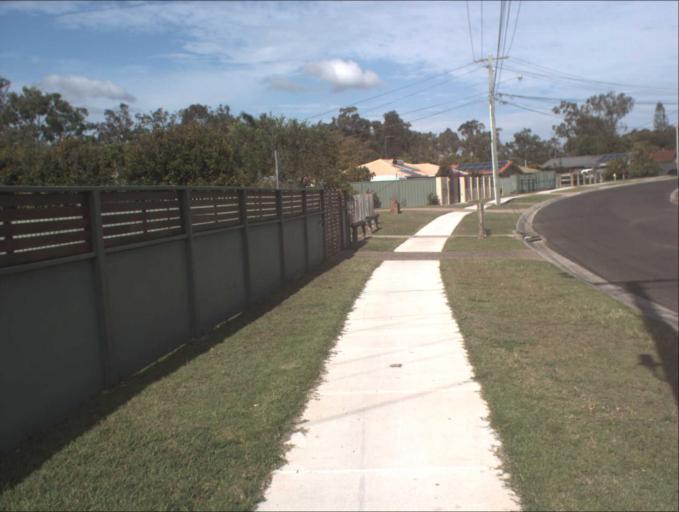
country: AU
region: Queensland
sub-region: Logan
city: Park Ridge South
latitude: -27.6736
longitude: 153.0416
